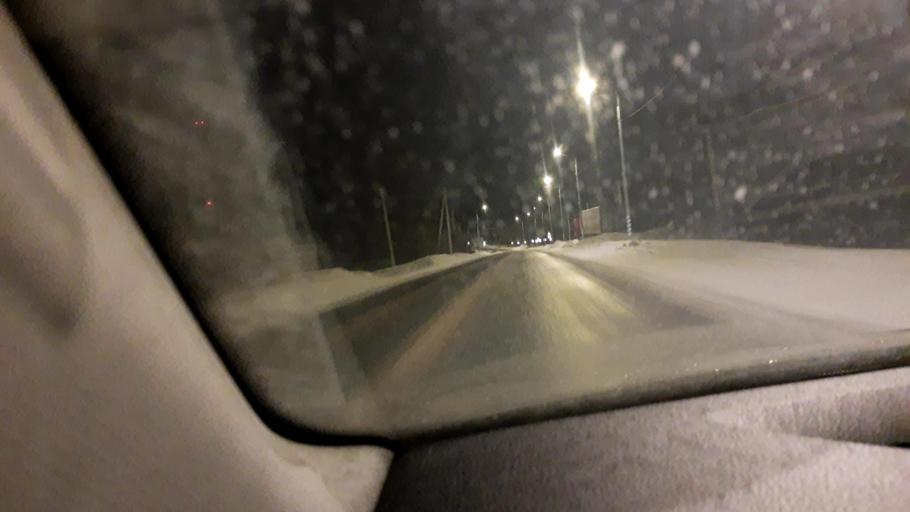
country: RU
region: Moskovskaya
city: Bogorodskoye
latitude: 56.5559
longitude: 38.1475
